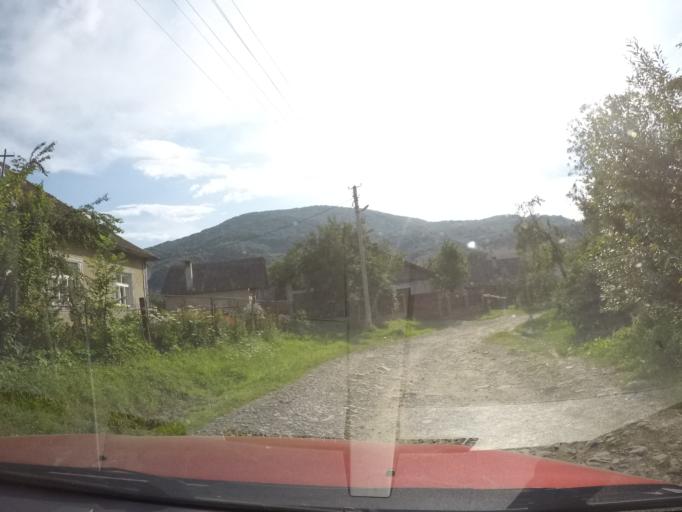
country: UA
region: Zakarpattia
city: Velykyi Bereznyi
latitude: 49.0154
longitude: 22.6240
